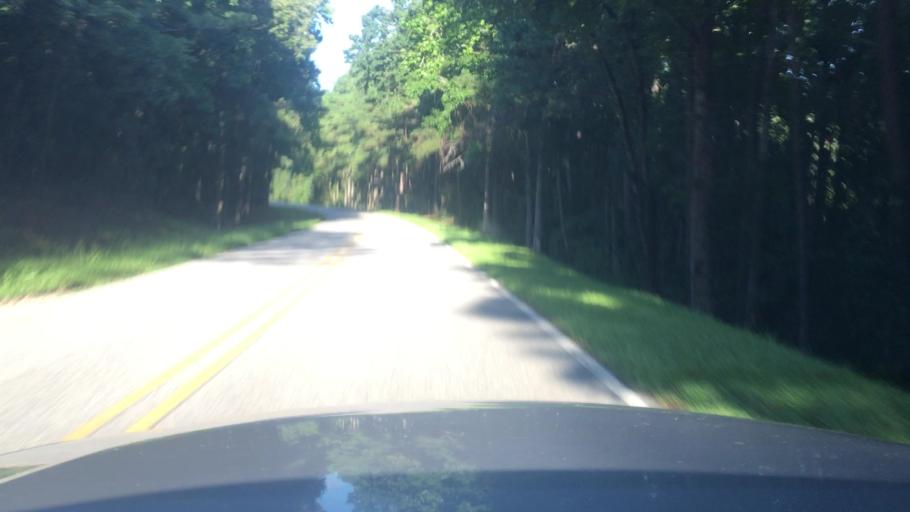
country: US
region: North Carolina
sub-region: Harnett County
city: Walkertown
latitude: 35.2269
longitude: -78.8861
